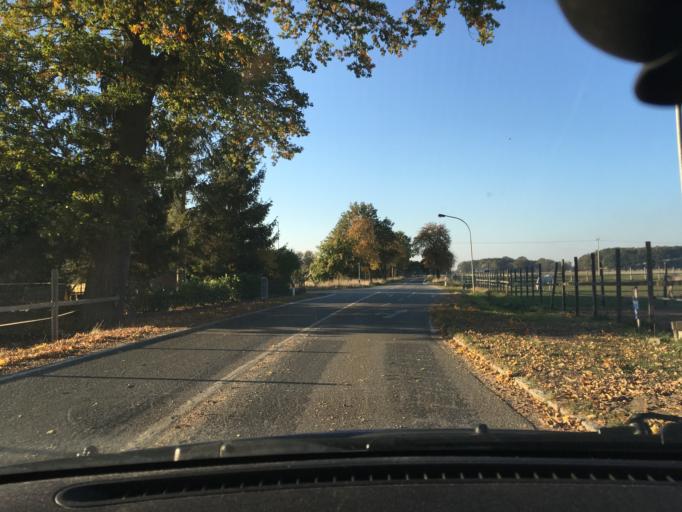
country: DE
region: Lower Saxony
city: Neu Darchau
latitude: 53.2882
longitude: 10.8747
